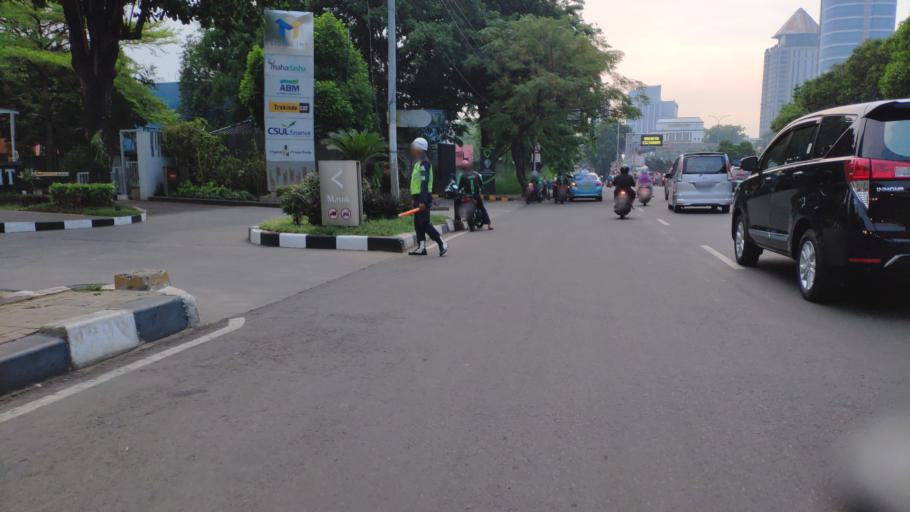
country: ID
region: Jakarta Raya
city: Jakarta
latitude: -6.2926
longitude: 106.8152
